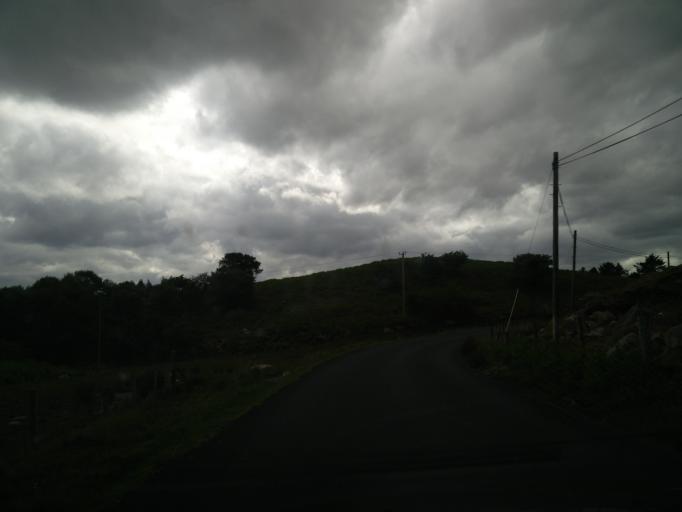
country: IE
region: Connaught
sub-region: Maigh Eo
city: Westport
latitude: 53.9193
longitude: -9.5559
